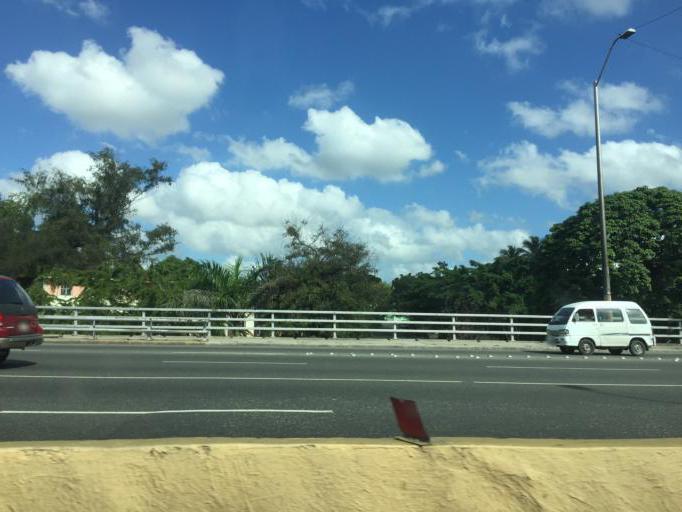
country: DO
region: Nacional
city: San Carlos
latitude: 18.4862
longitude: -69.8787
